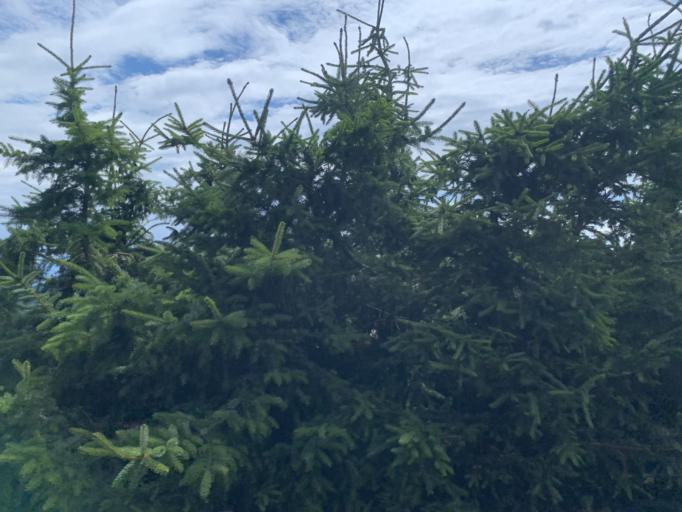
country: IT
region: Trentino-Alto Adige
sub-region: Bolzano
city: Soprabolzano
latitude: 46.5282
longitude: 11.4076
